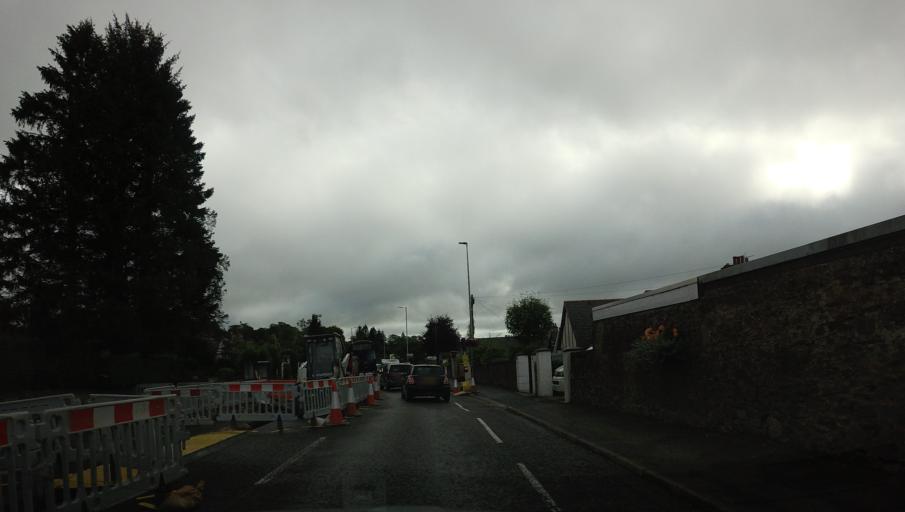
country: GB
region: Scotland
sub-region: Aberdeenshire
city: Westhill
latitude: 57.0972
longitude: -2.2564
